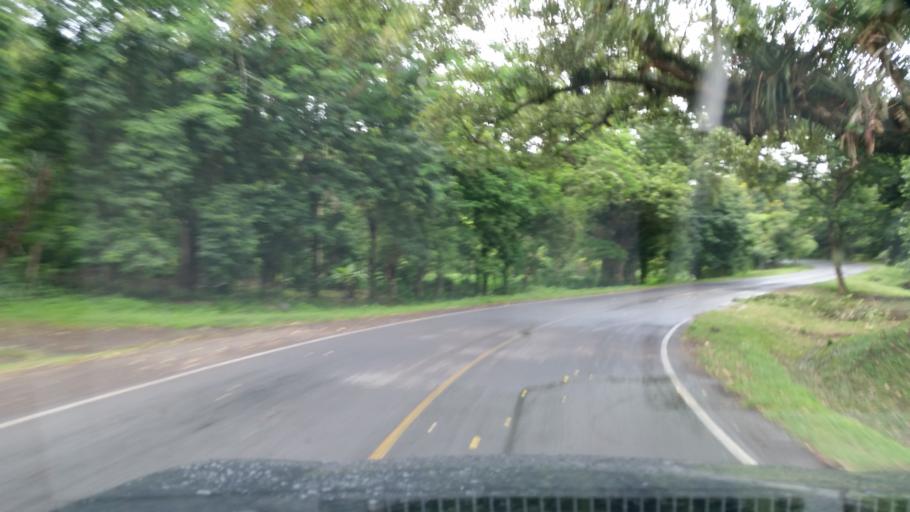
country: NI
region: Matagalpa
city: San Ramon
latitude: 13.0462
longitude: -85.7684
